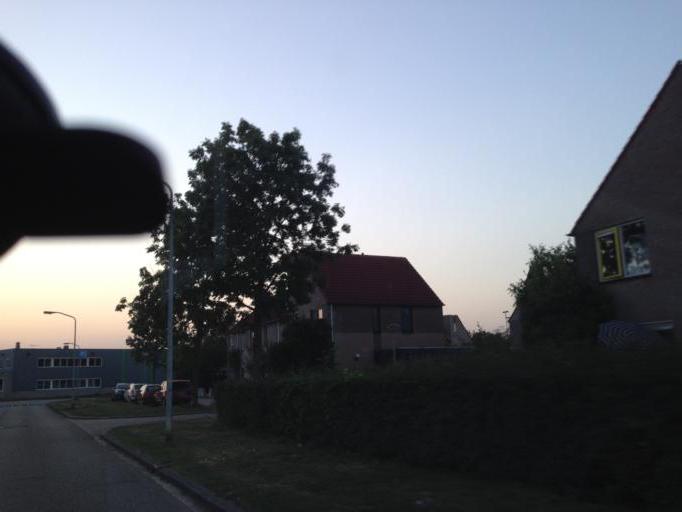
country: NL
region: Flevoland
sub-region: Gemeente Almere
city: Almere Stad
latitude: 52.3619
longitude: 5.2038
